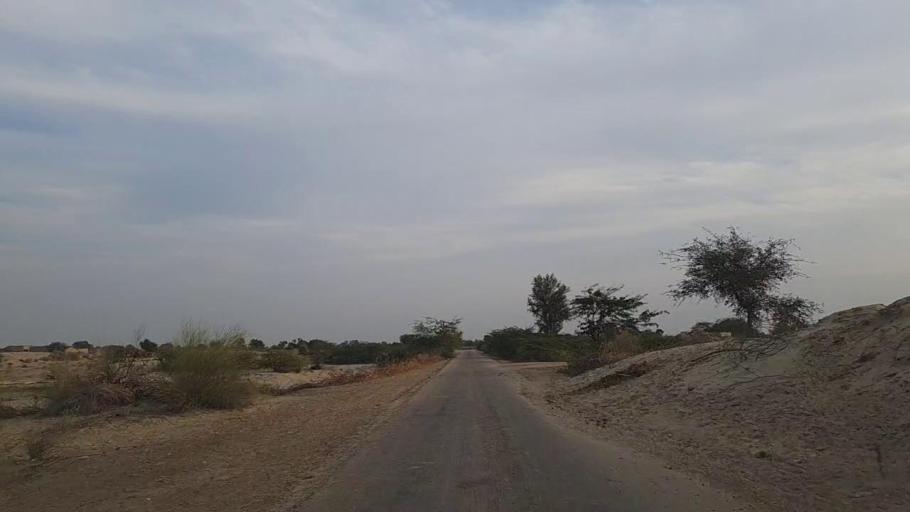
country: PK
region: Sindh
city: Jam Sahib
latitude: 26.4799
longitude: 68.5628
